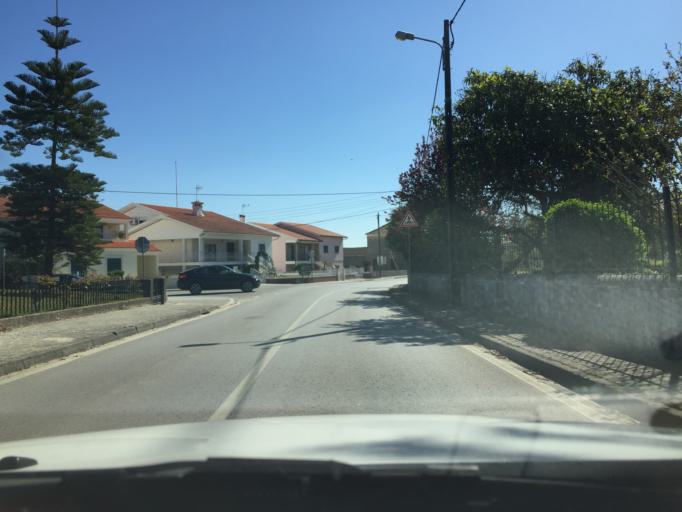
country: PT
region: Aveiro
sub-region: Anadia
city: Sangalhos
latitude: 40.4217
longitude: -8.5307
